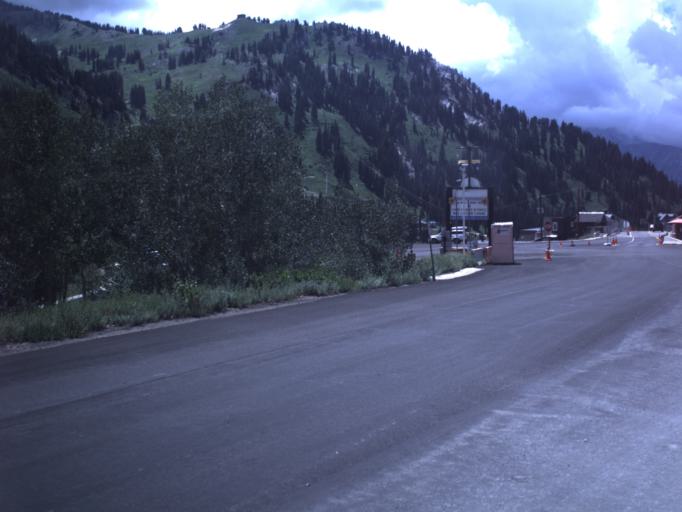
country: US
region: Utah
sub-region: Summit County
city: Snyderville
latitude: 40.5923
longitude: -111.6305
